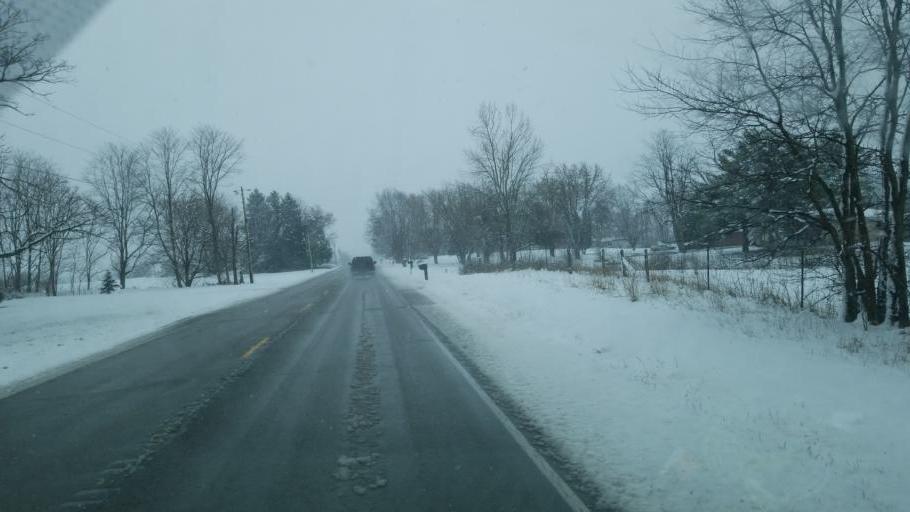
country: US
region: Indiana
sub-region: Delaware County
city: Muncie
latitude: 40.1085
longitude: -85.3199
